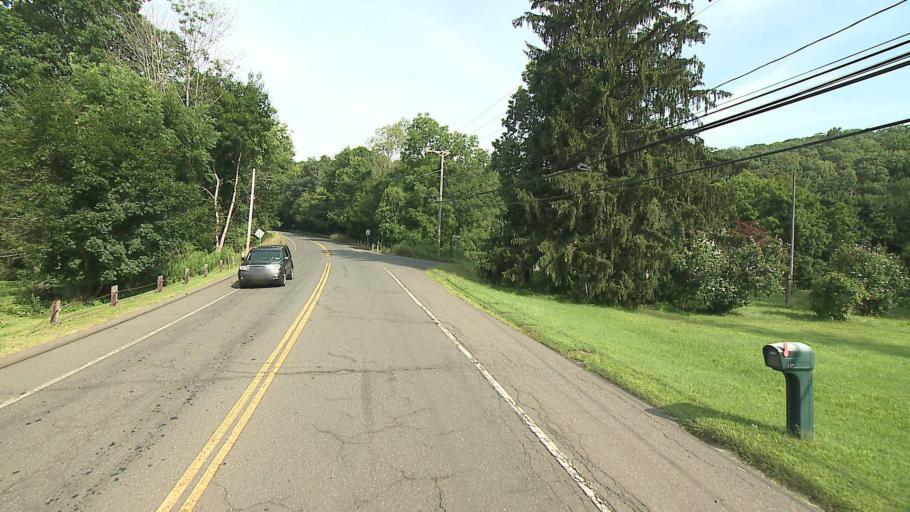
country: US
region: New York
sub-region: Putnam County
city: Putnam Lake
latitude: 41.4723
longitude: -73.4934
